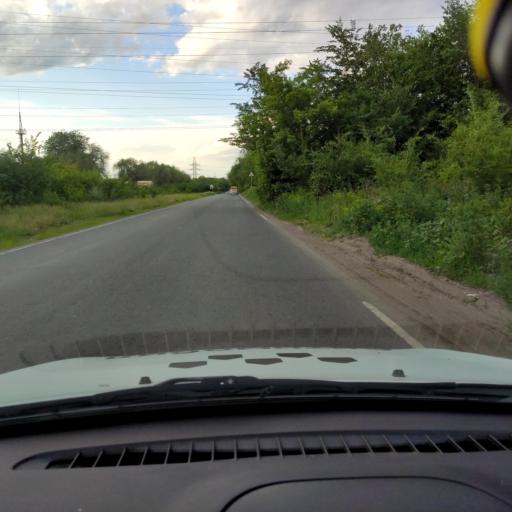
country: RU
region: Samara
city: Tol'yatti
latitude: 53.5775
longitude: 49.2553
